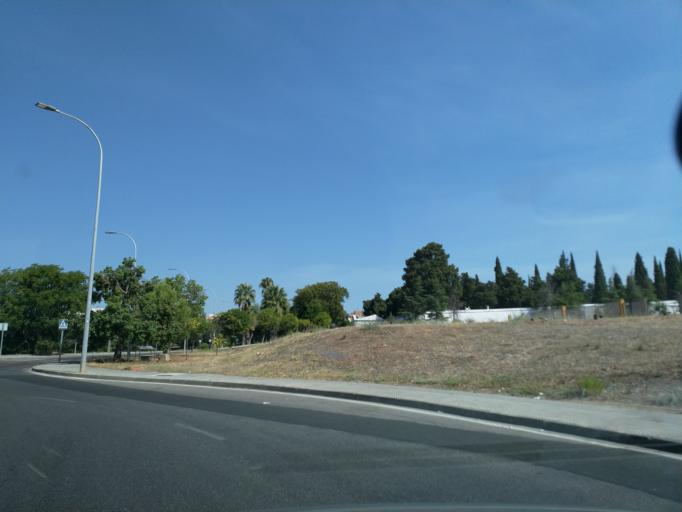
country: ES
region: Extremadura
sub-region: Provincia de Badajoz
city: Merida
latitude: 38.9299
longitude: -6.3471
